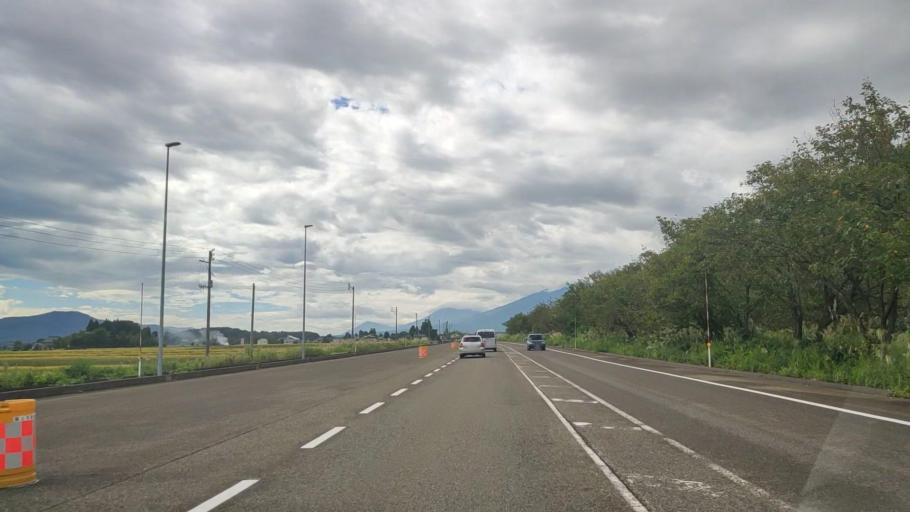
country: JP
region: Niigata
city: Arai
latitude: 37.0425
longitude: 138.2378
